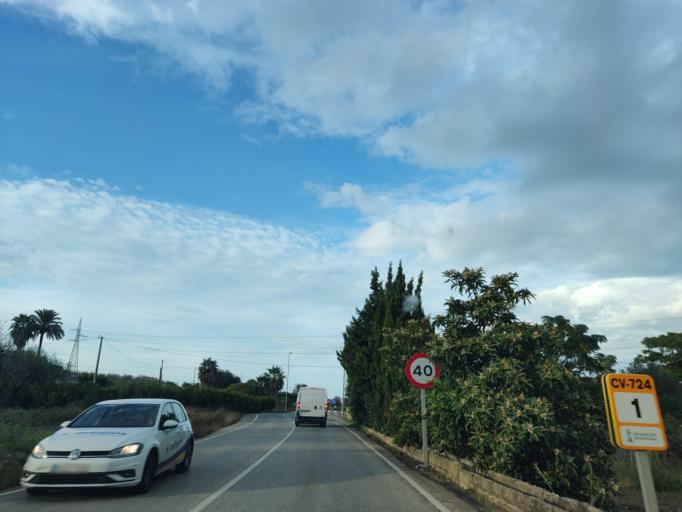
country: ES
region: Valencia
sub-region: Provincia de Alicante
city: Pedreguer
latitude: 38.8060
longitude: 0.0338
